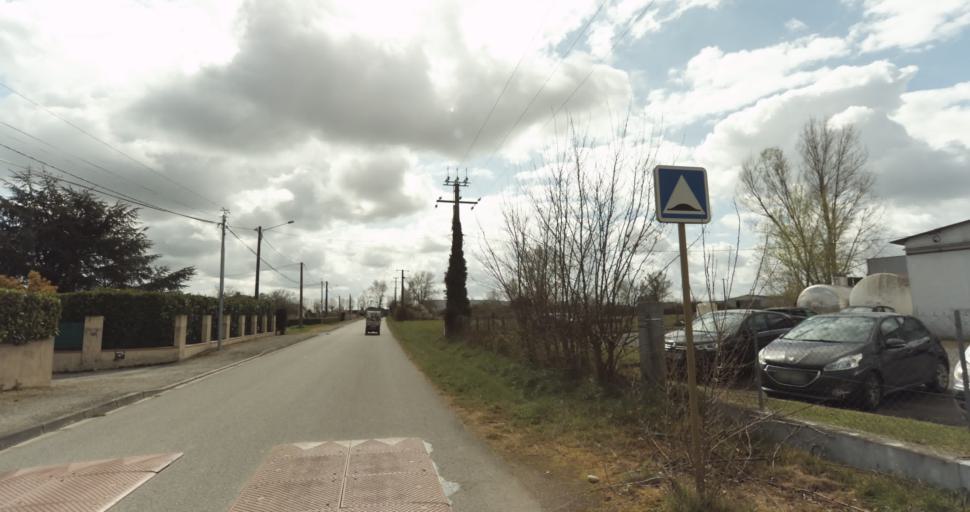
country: FR
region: Midi-Pyrenees
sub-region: Departement de la Haute-Garonne
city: Auterive
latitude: 43.3647
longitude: 1.4627
